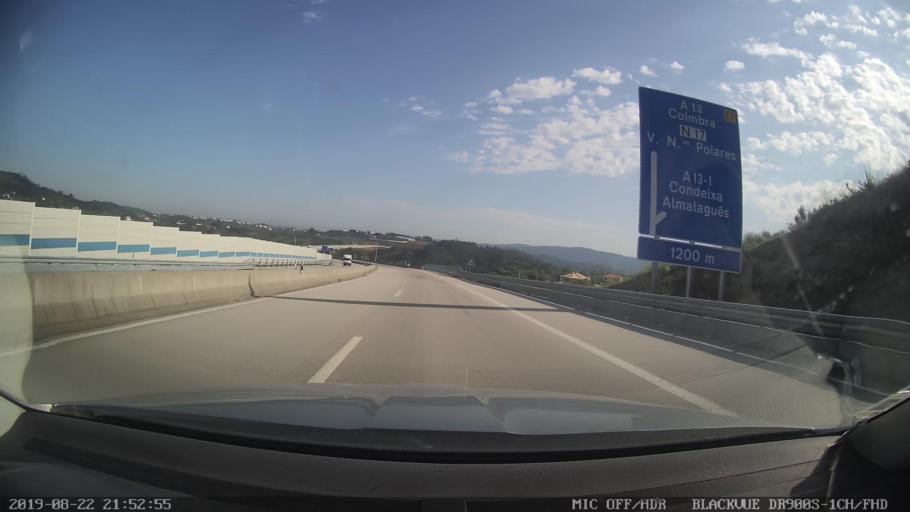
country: PT
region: Coimbra
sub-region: Miranda do Corvo
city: Miranda do Corvo
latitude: 40.1076
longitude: -8.3905
